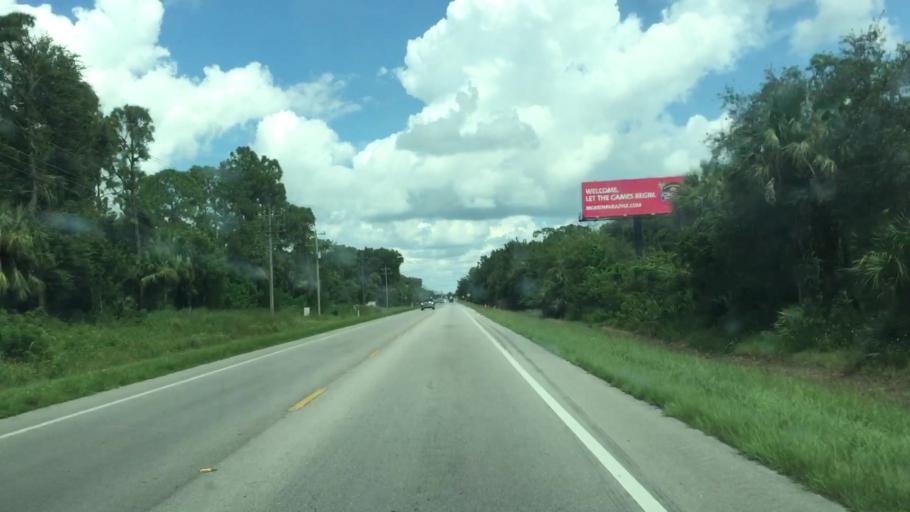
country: US
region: Florida
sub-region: Collier County
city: Immokalee
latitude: 26.4015
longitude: -81.4171
